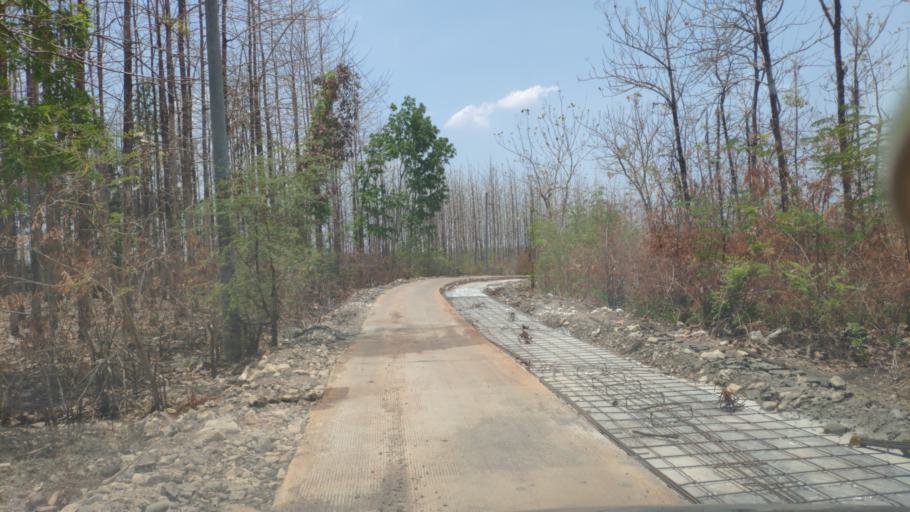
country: ID
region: Central Java
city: Randublatung
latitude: -7.2687
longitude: 111.3792
